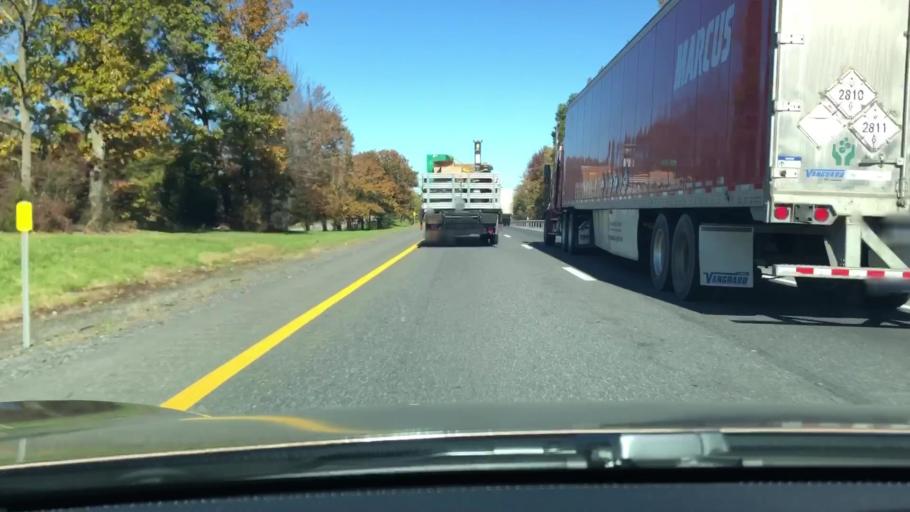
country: US
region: New York
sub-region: Ulster County
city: Plattekill
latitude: 41.6007
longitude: -74.0844
